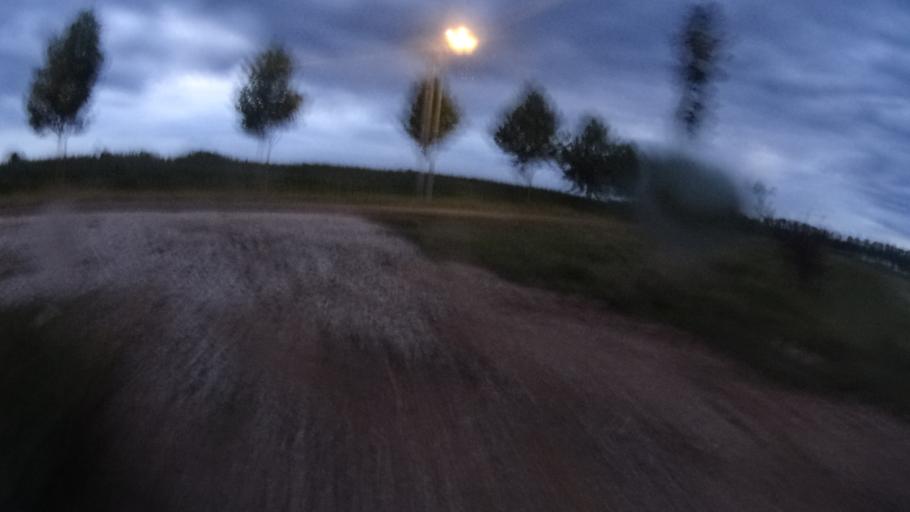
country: PL
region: Masovian Voivodeship
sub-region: Powiat warszawski zachodni
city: Ozarow Mazowiecki
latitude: 52.2322
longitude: 20.7968
